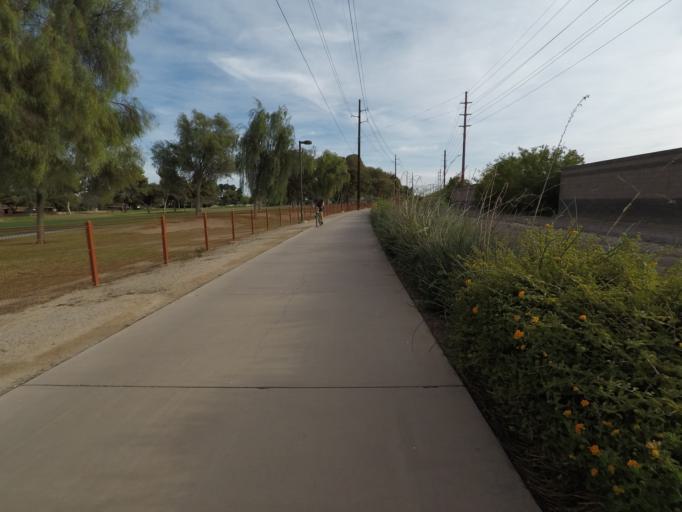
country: US
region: Arizona
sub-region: Maricopa County
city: Guadalupe
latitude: 33.3515
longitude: -111.9381
